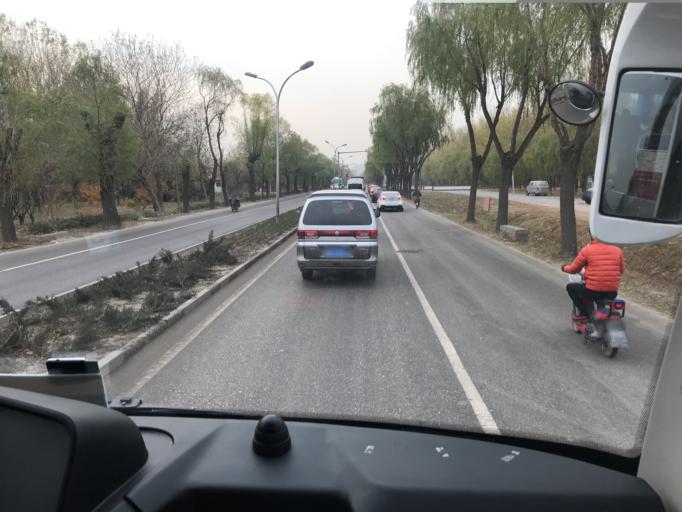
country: CN
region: Beijing
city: Wenquan
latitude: 40.0875
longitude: 116.2100
